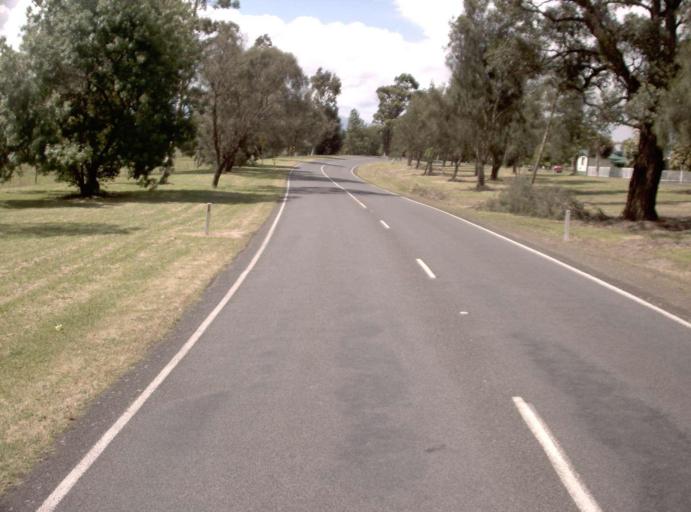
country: AU
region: Victoria
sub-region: Latrobe
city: Moe
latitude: -38.1748
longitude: 146.2988
